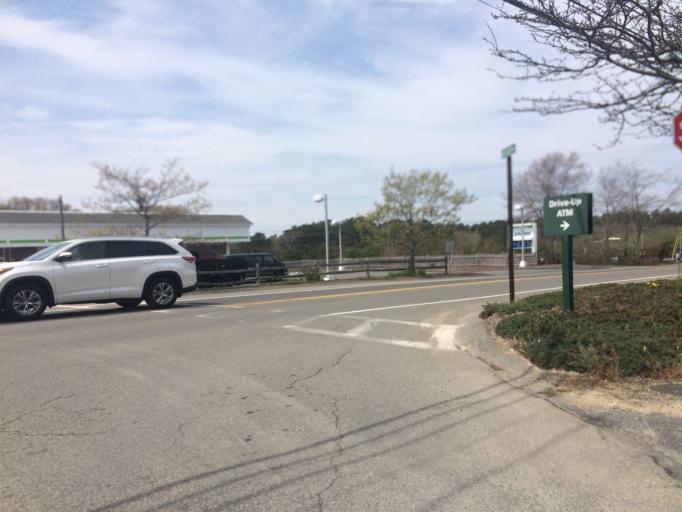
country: US
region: Massachusetts
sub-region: Barnstable County
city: Provincetown
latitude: 42.0534
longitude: -70.1955
